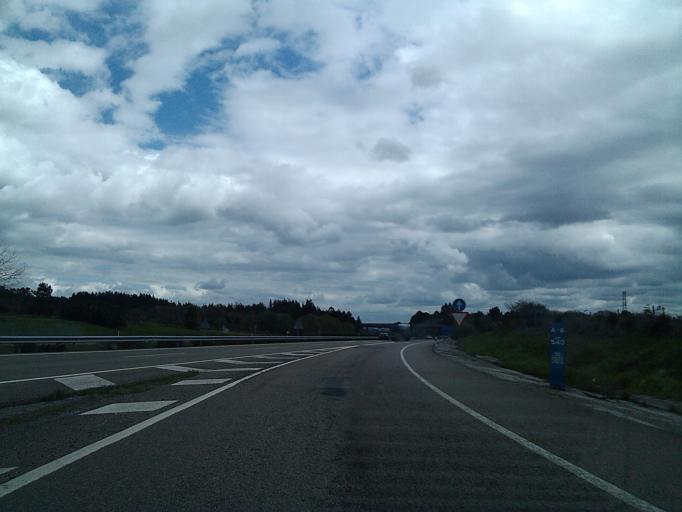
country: ES
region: Galicia
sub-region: Provincia de Lugo
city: Guitiriz
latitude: 43.1934
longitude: -7.9527
